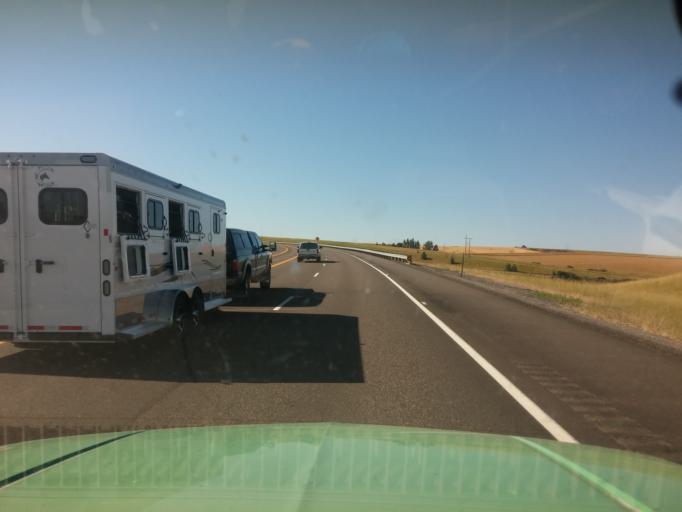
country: US
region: Washington
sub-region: Asotin County
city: Clarkston
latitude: 46.4782
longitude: -117.0387
